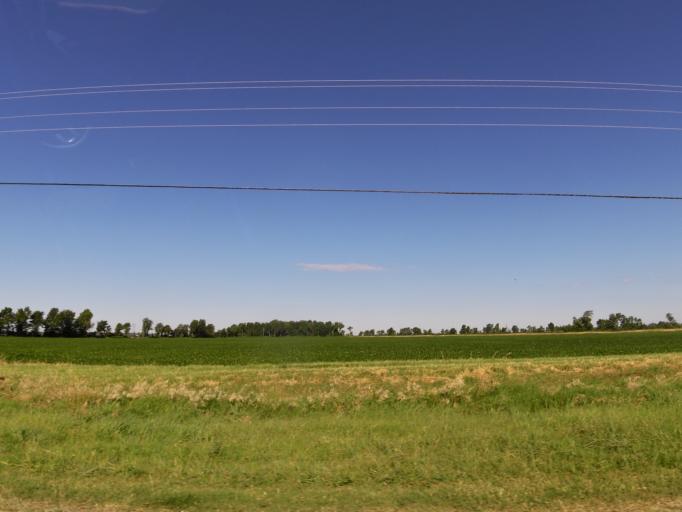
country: US
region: Arkansas
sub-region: Clay County
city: Corning
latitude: 36.4351
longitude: -90.5859
